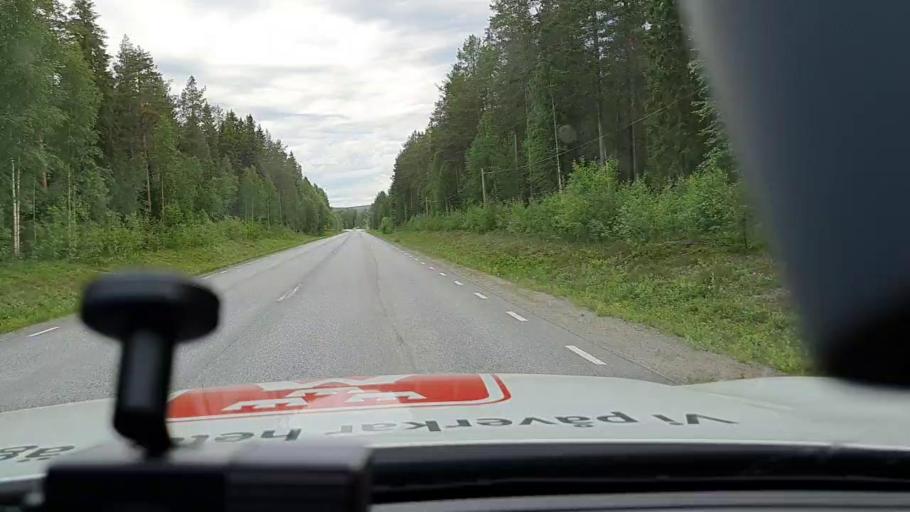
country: SE
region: Norrbotten
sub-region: Bodens Kommun
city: Boden
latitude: 65.8089
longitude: 21.6539
